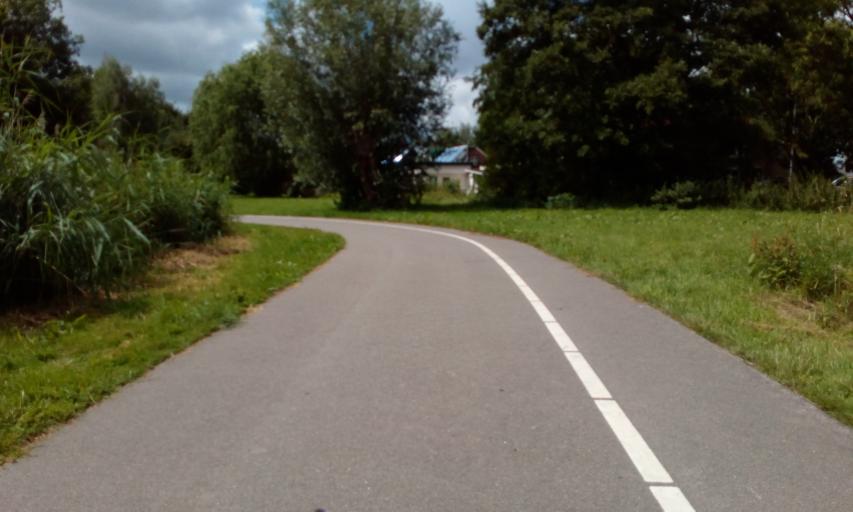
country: NL
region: South Holland
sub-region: Gemeente Binnenmaas
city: Heinenoord
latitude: 51.8674
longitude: 4.4896
